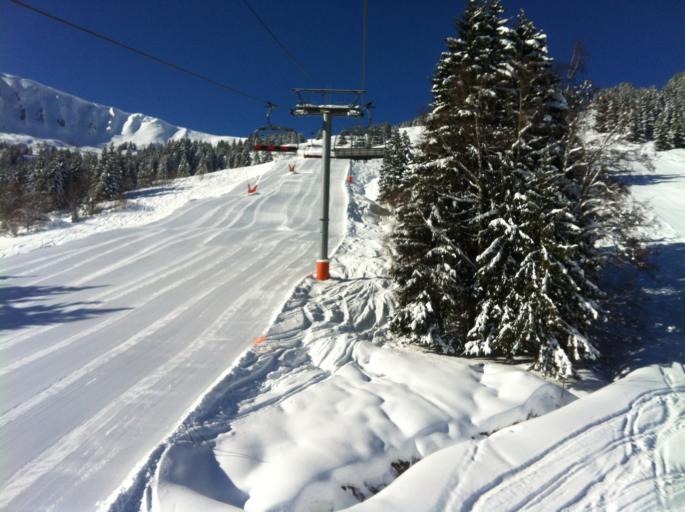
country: FR
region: Rhone-Alpes
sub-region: Departement de la Haute-Savoie
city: Les Contamines-Montjoie
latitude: 45.8510
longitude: 6.6968
